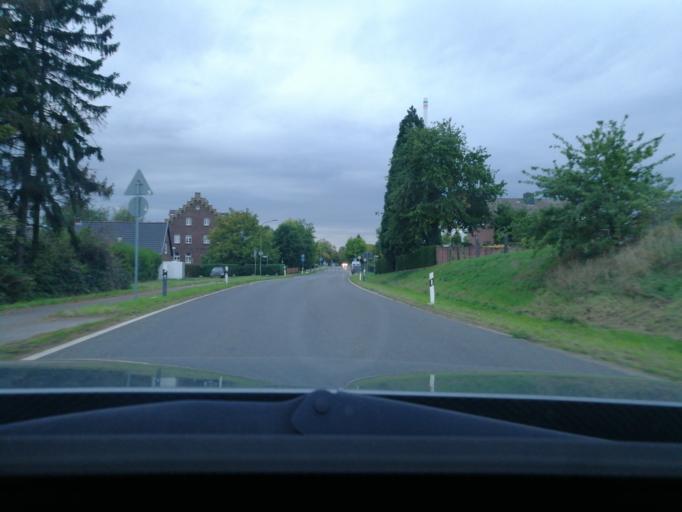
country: DE
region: North Rhine-Westphalia
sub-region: Regierungsbezirk Dusseldorf
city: Dormagen
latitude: 51.1349
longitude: 6.7511
